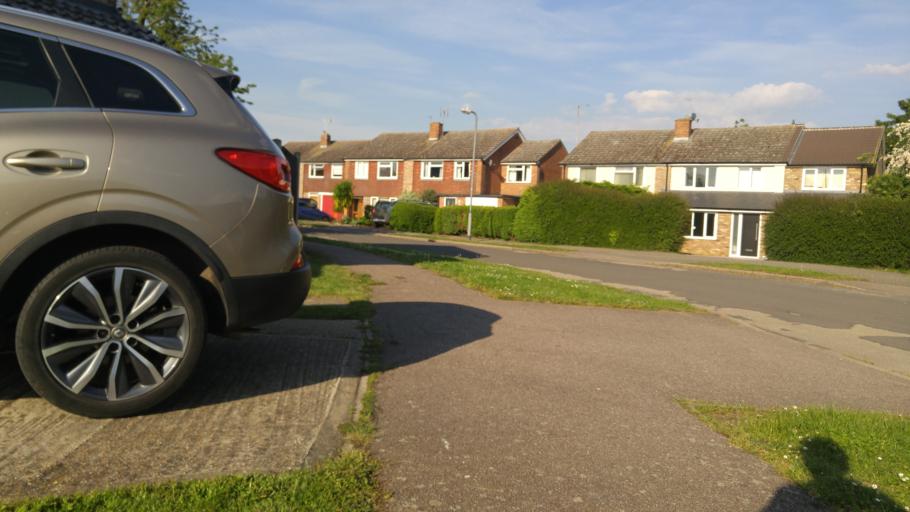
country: GB
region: England
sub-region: Essex
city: Eight Ash Green
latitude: 51.9187
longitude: 0.8009
